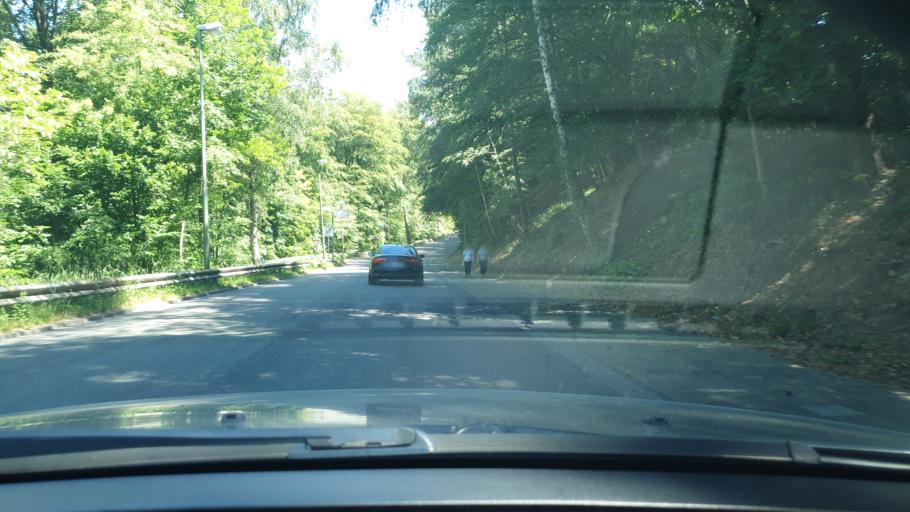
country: DE
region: Rheinland-Pfalz
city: Kaiserslautern
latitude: 49.4521
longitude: 7.7422
